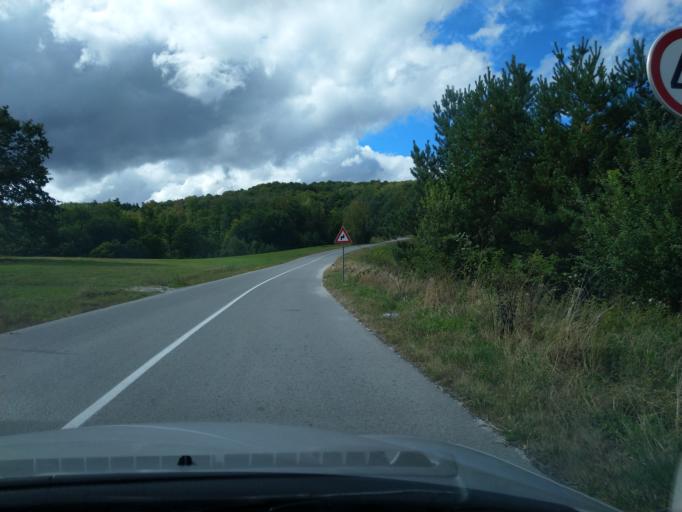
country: RS
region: Central Serbia
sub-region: Zlatiborski Okrug
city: Cajetina
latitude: 43.7184
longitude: 19.7870
